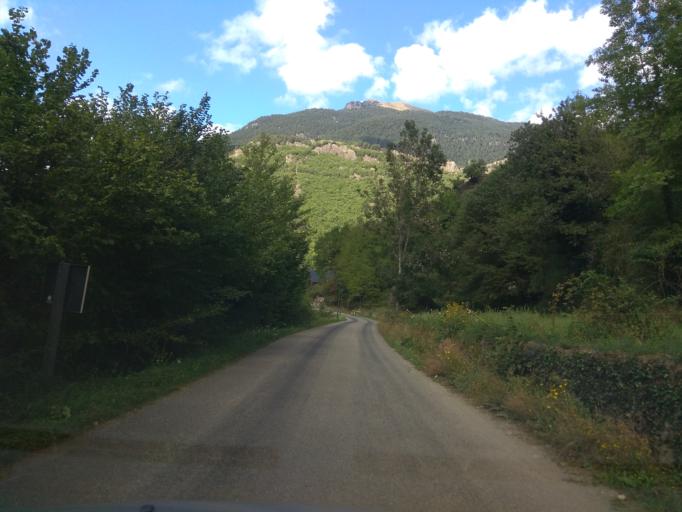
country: ES
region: Catalonia
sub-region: Provincia de Lleida
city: Les
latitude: 42.7354
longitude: 0.7203
